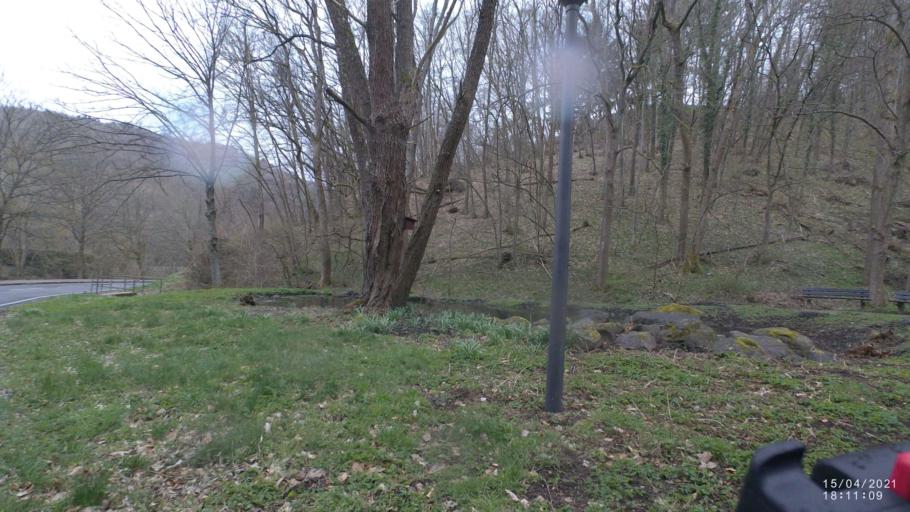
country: DE
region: Rheinland-Pfalz
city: Volkesfeld
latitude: 50.3858
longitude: 7.1501
